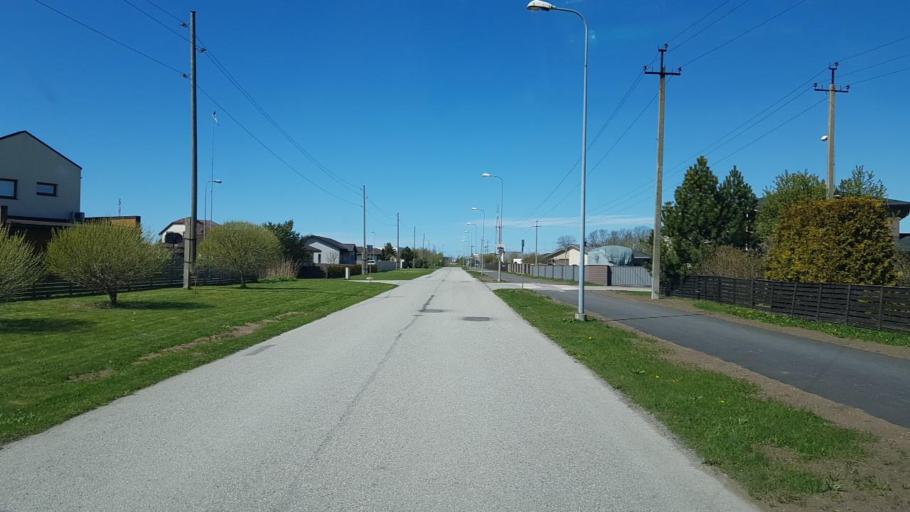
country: EE
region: Harju
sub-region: Viimsi vald
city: Viimsi
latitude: 59.5057
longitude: 24.8545
